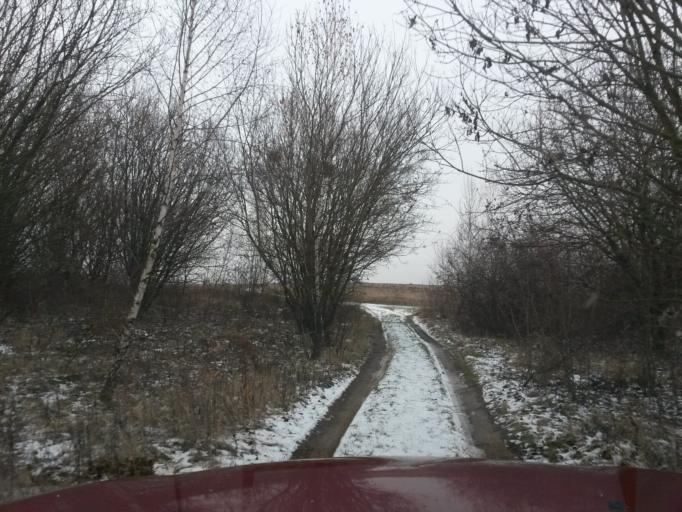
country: SK
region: Kosicky
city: Kosice
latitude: 48.7219
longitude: 21.2826
